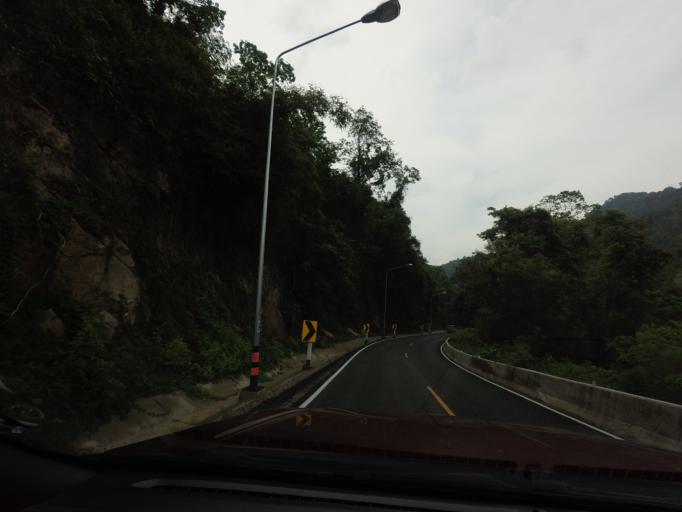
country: TH
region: Yala
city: Than To
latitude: 6.1347
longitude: 101.2985
